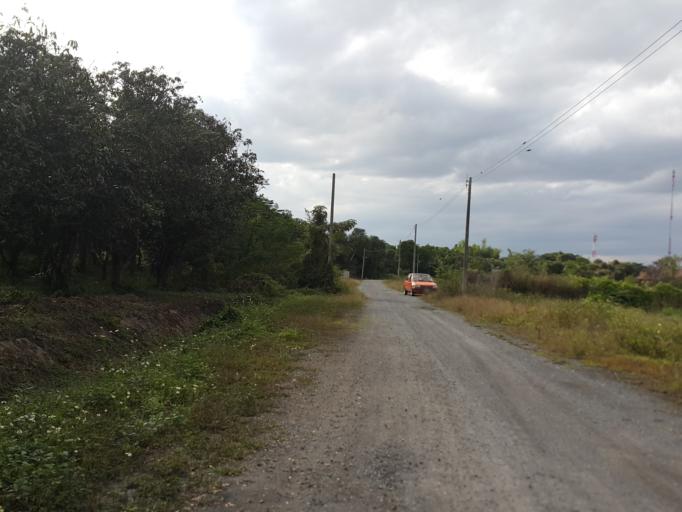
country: TH
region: Chiang Mai
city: San Sai
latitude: 18.8900
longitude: 99.0980
